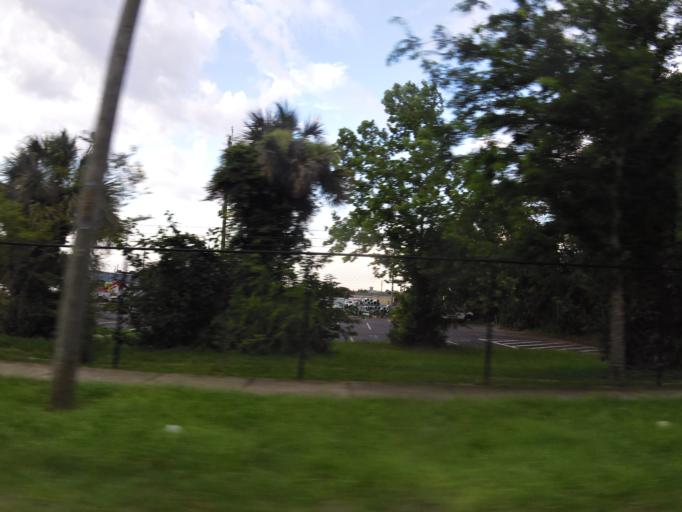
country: US
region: Florida
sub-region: Duval County
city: Jacksonville
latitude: 30.3517
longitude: -81.6612
